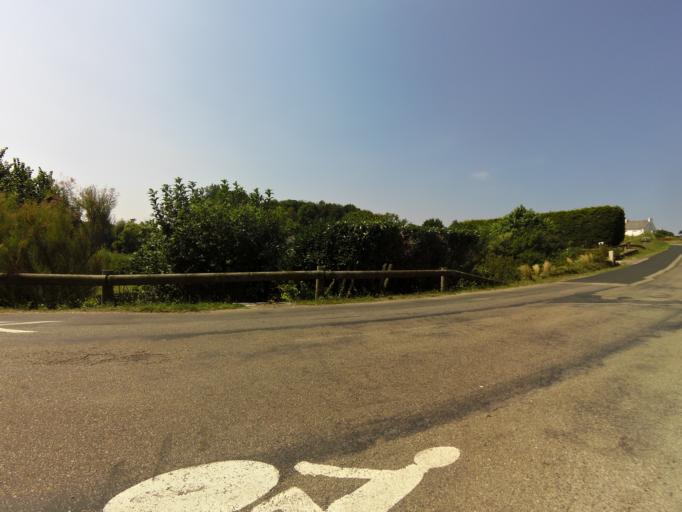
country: FR
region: Brittany
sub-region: Departement du Finistere
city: Pouldreuzic
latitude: 47.9133
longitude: -4.3530
